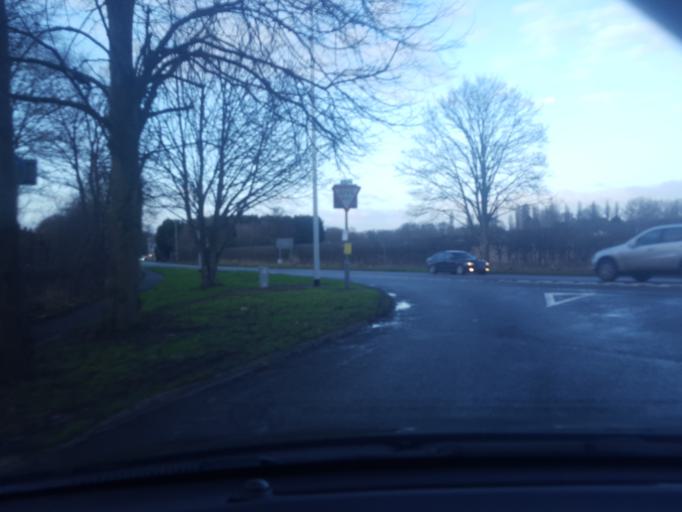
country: GB
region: England
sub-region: Shropshire
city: Tong
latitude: 52.6451
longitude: -2.2902
